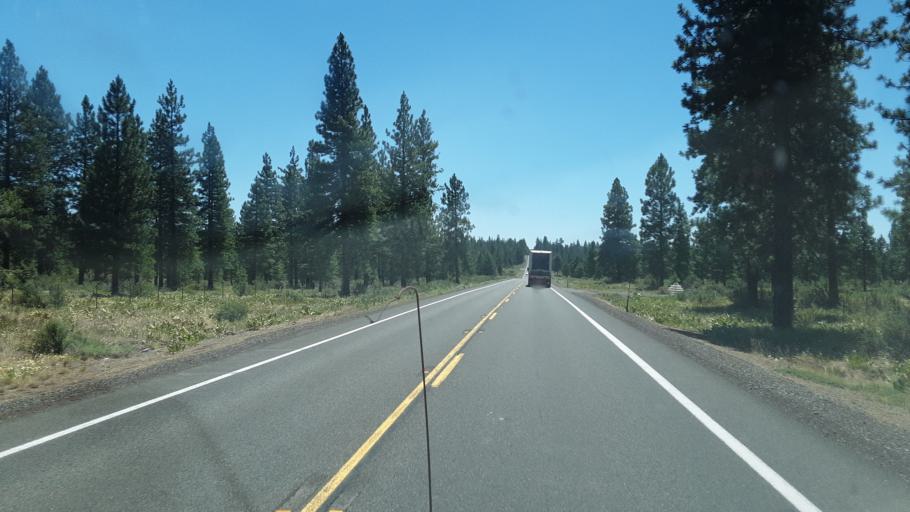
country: US
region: California
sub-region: Siskiyou County
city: Tulelake
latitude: 41.5784
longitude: -121.1875
